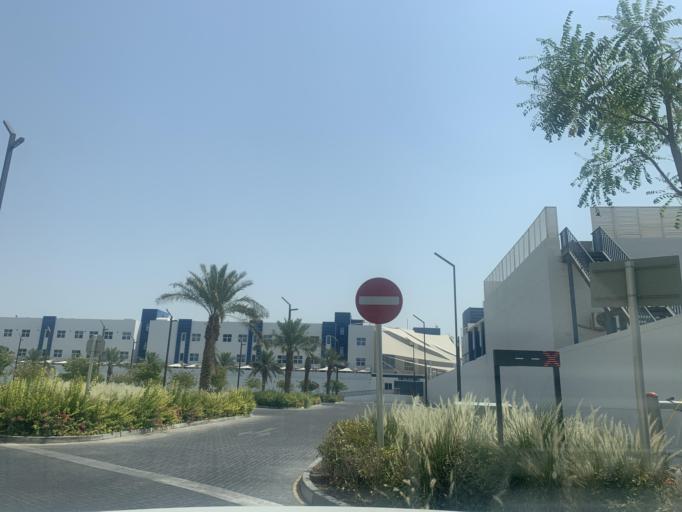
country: BH
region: Central Governorate
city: Madinat Hamad
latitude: 26.1617
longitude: 50.4704
